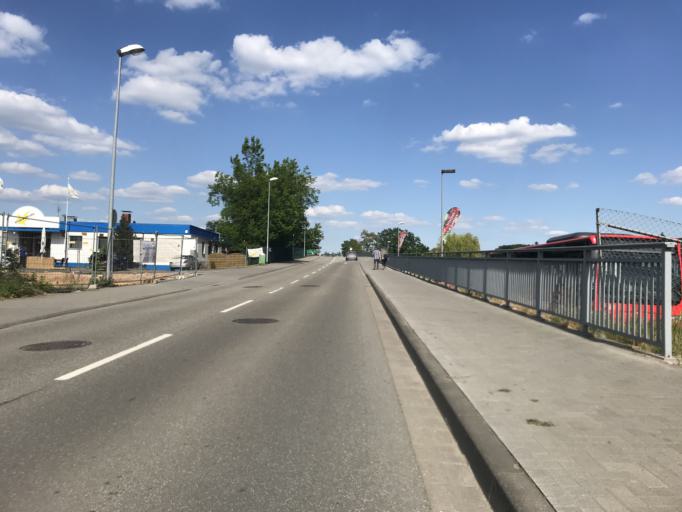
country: DE
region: Rheinland-Pfalz
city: Ingelheim am Rhein
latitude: 49.9798
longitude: 8.0561
